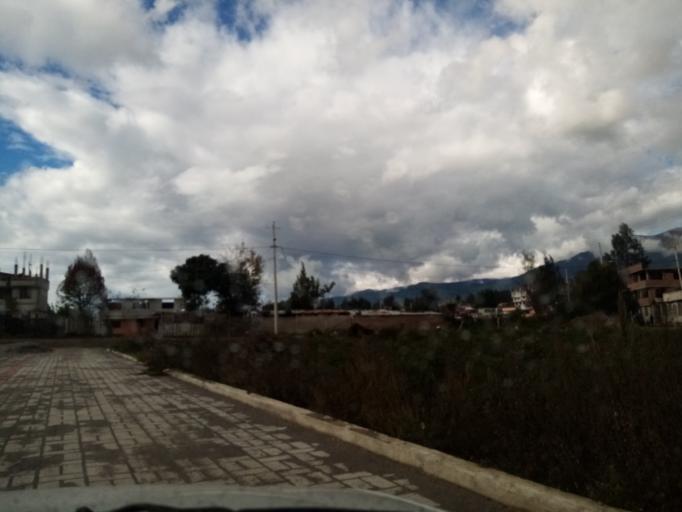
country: EC
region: Chimborazo
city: Riobamba
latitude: -1.6875
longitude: -78.6230
